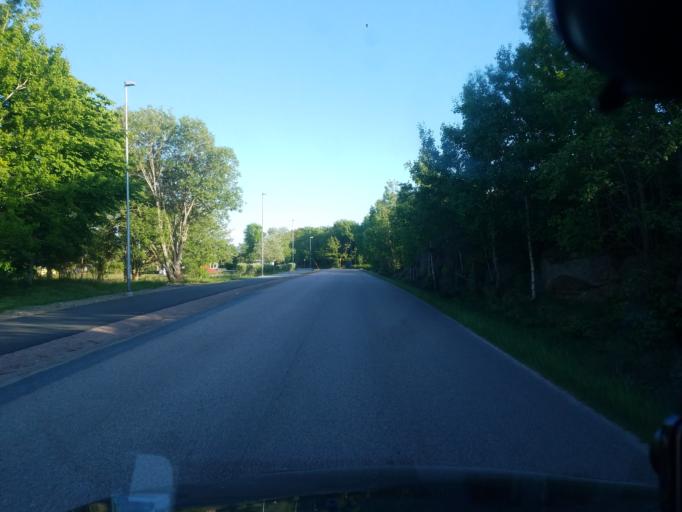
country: SE
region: Vaestra Goetaland
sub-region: Lysekils Kommun
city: Lysekil
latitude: 58.2905
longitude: 11.4572
